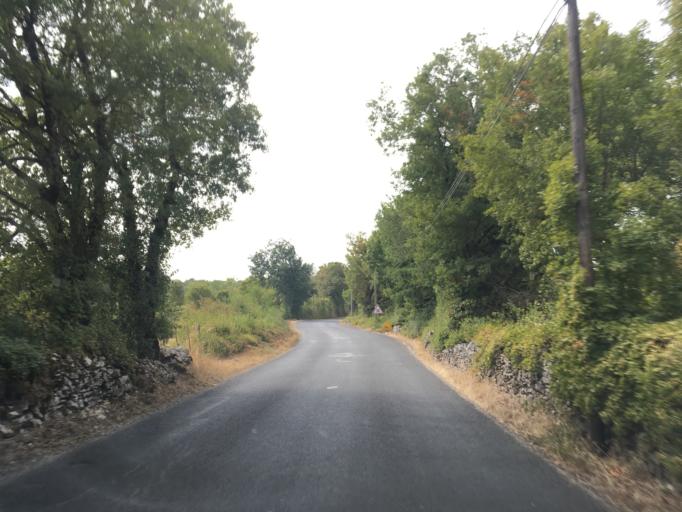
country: FR
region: Midi-Pyrenees
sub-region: Departement du Lot
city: Gramat
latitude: 44.8080
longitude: 1.6207
